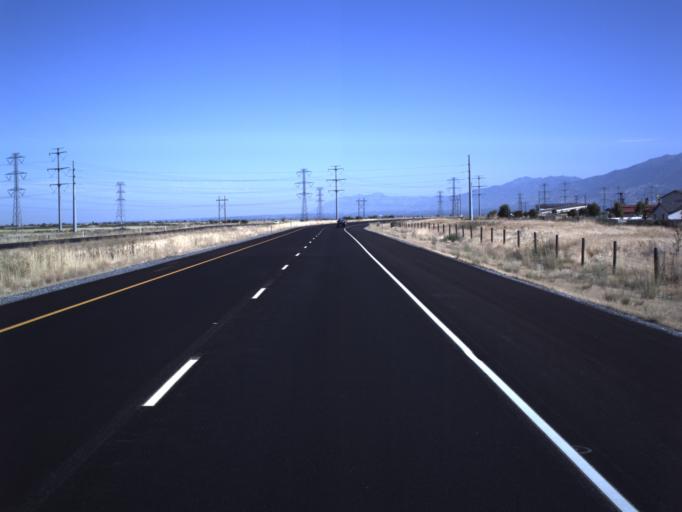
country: US
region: Utah
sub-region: Davis County
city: North Salt Lake
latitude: 40.8585
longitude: -111.9437
